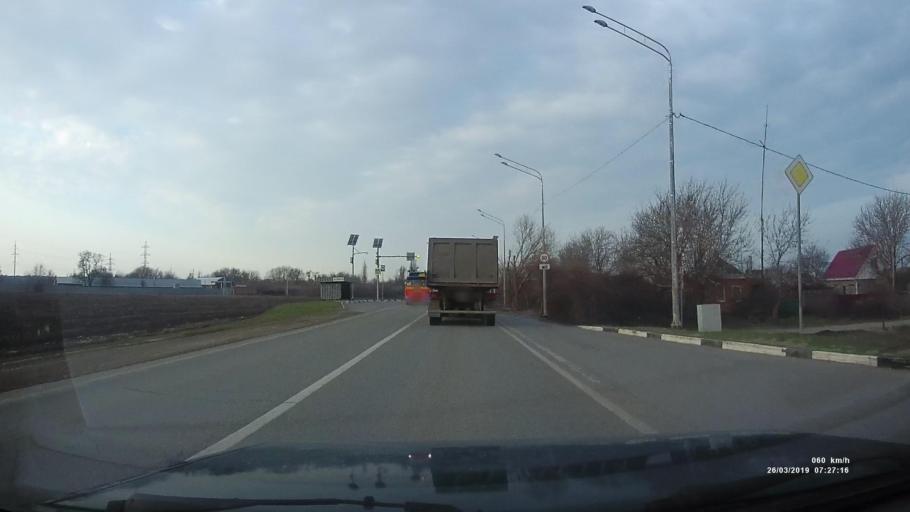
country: RU
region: Rostov
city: Taganrog
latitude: 47.2635
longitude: 38.8299
